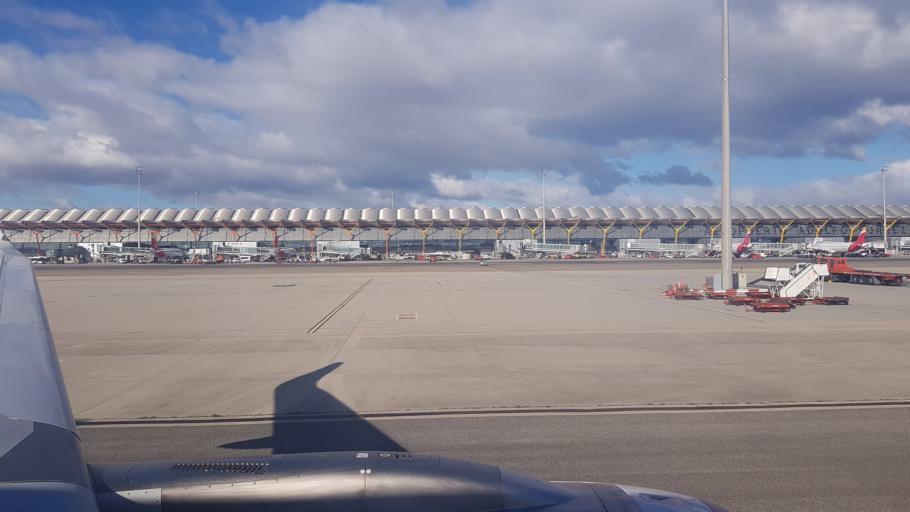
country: ES
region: Madrid
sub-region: Provincia de Madrid
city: Barajas de Madrid
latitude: 40.4888
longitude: -3.5865
